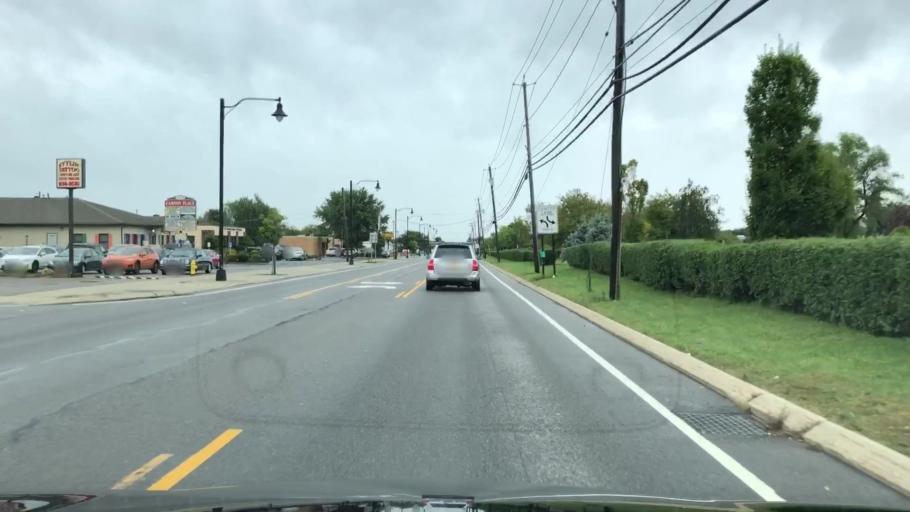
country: US
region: New York
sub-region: Erie County
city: Eggertsville
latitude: 42.9375
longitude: -78.7842
